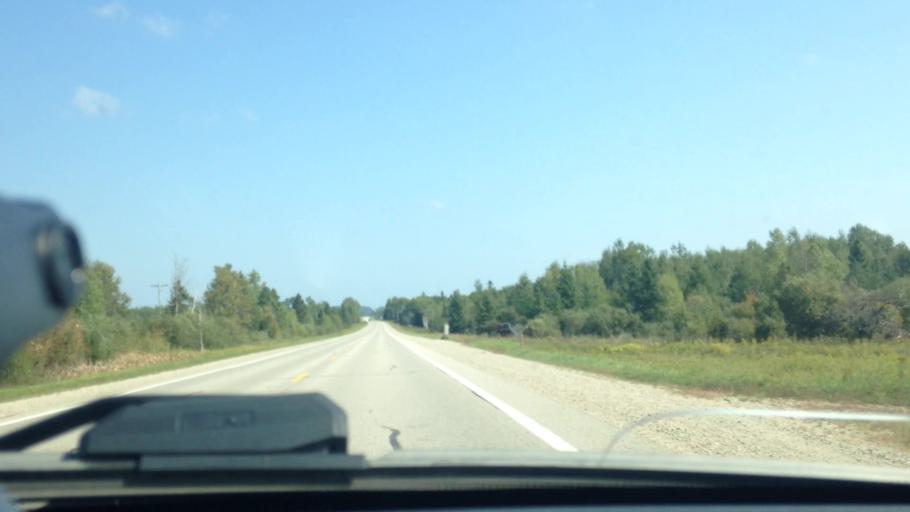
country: US
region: Michigan
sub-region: Luce County
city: Newberry
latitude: 46.3102
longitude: -85.6237
